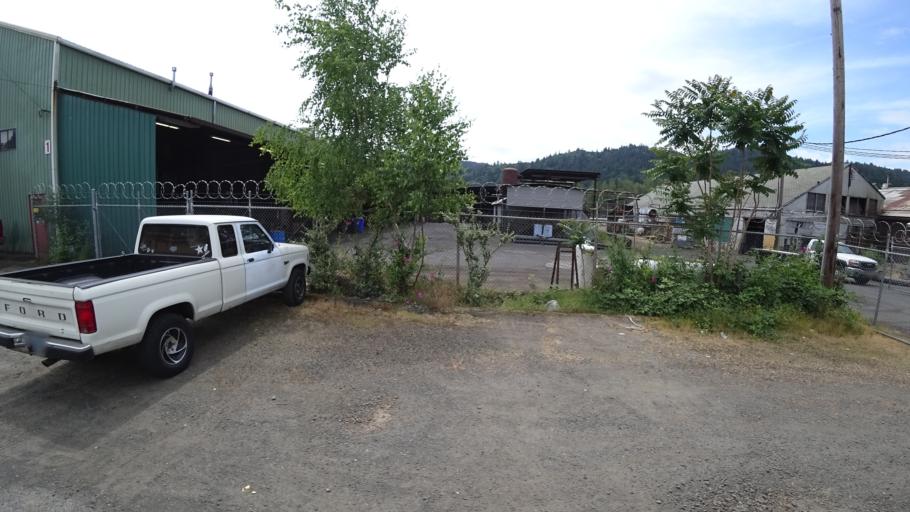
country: US
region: Oregon
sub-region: Washington County
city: West Haven
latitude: 45.5854
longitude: -122.7568
